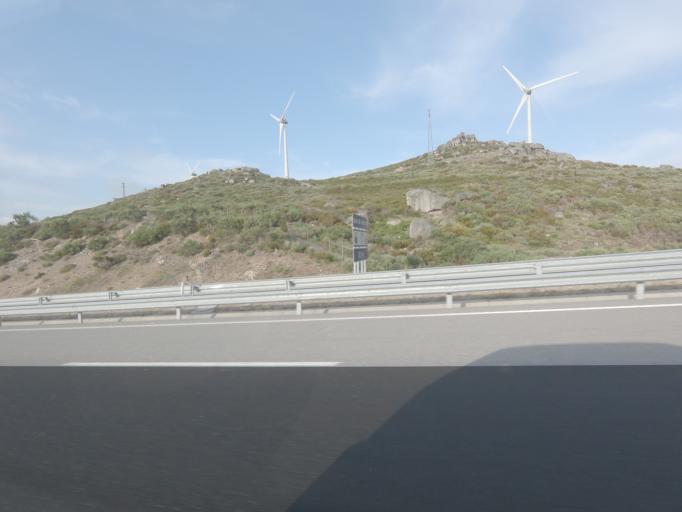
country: PT
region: Vila Real
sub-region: Vila Pouca de Aguiar
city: Vila Pouca de Aguiar
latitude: 41.4469
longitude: -7.6479
